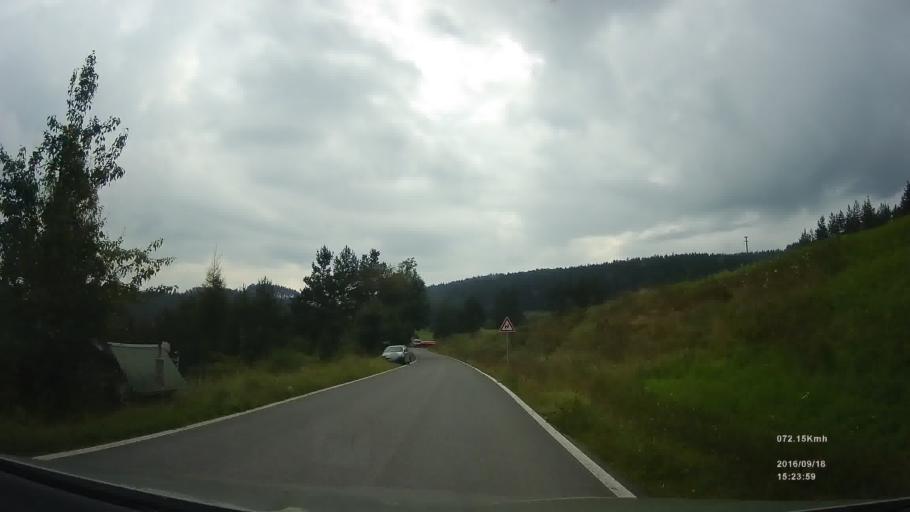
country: SK
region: Presovsky
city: Lubica
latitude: 49.0365
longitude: 20.4897
